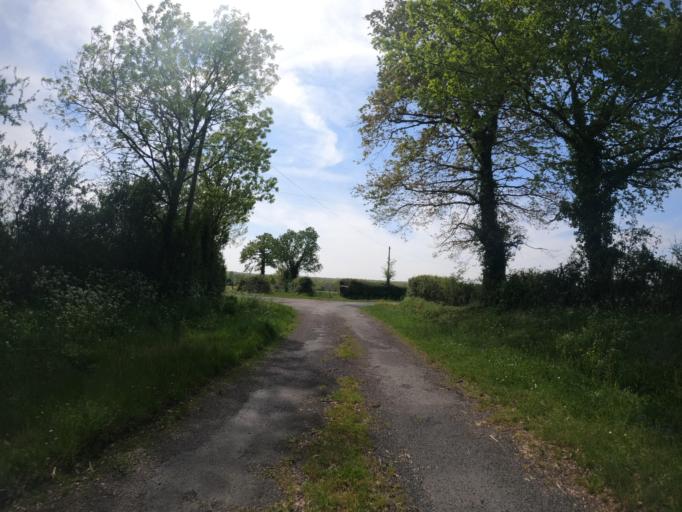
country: FR
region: Poitou-Charentes
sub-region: Departement des Deux-Sevres
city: La Chapelle-Saint-Laurent
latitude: 46.6551
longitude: -0.5161
